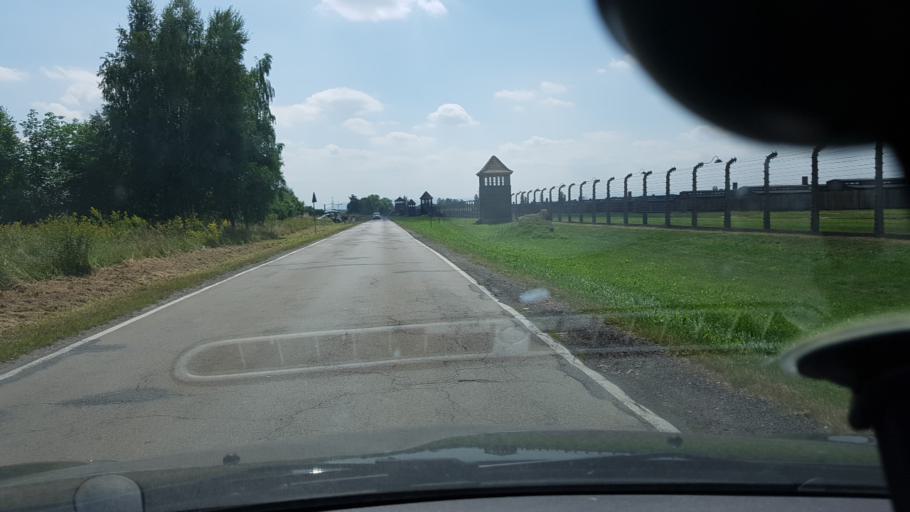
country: PL
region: Lesser Poland Voivodeship
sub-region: Powiat oswiecimski
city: Brzezinka
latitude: 50.0393
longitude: 19.1813
